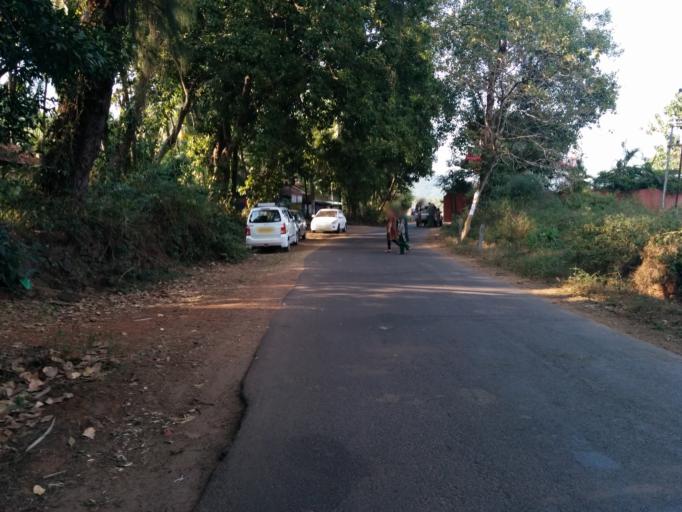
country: IN
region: Goa
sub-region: South Goa
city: Kankon
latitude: 15.0094
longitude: 74.0295
